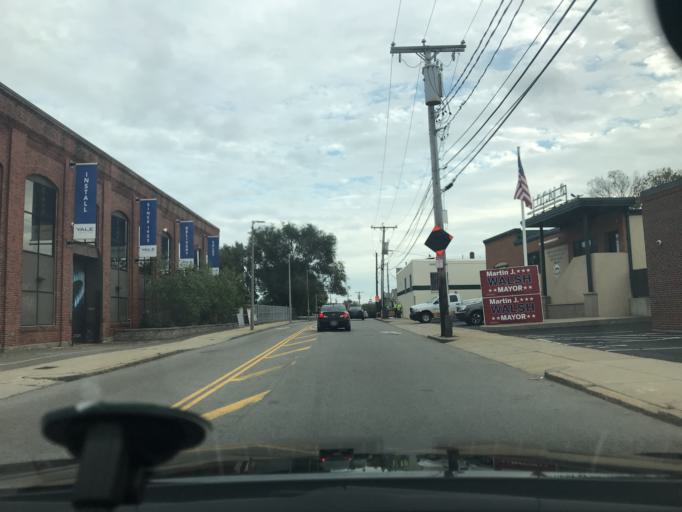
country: US
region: Massachusetts
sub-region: Suffolk County
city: South Boston
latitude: 42.3027
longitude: -71.0523
